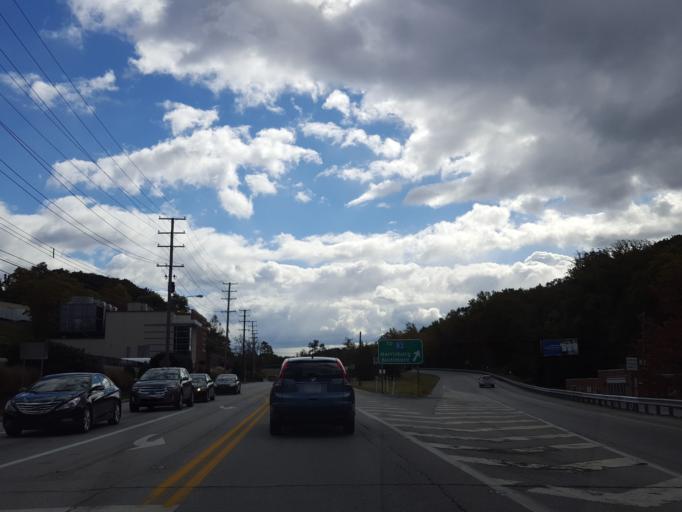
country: US
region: Pennsylvania
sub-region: York County
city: Grantley
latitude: 39.9450
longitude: -76.7196
